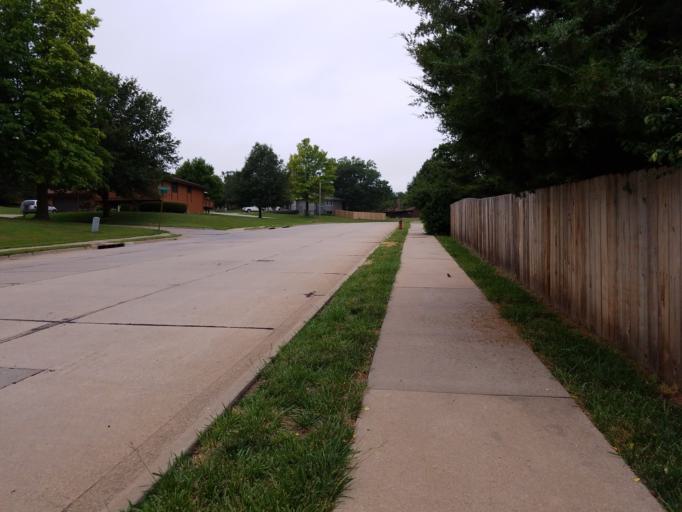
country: US
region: Kansas
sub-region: Riley County
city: Manhattan
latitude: 39.2049
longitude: -96.6235
